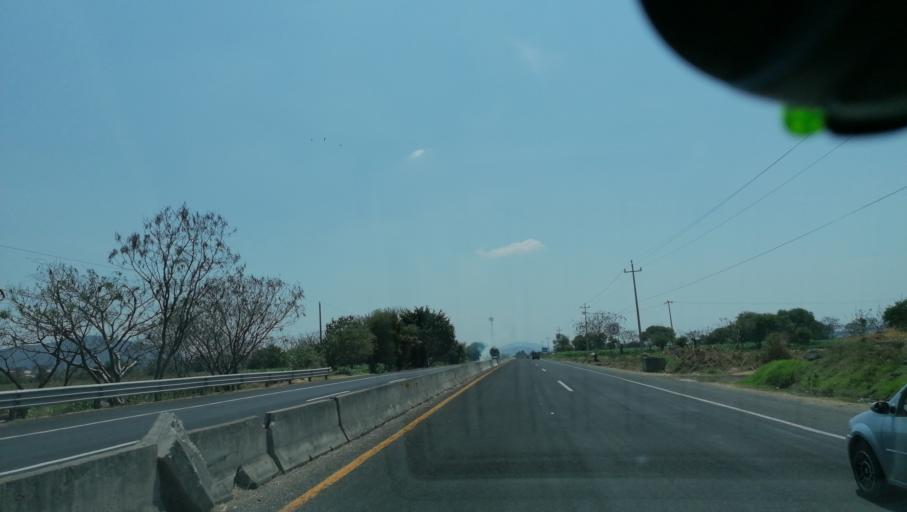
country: MX
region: Puebla
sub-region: Huaquechula
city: Tronconal
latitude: 18.8020
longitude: -98.4499
